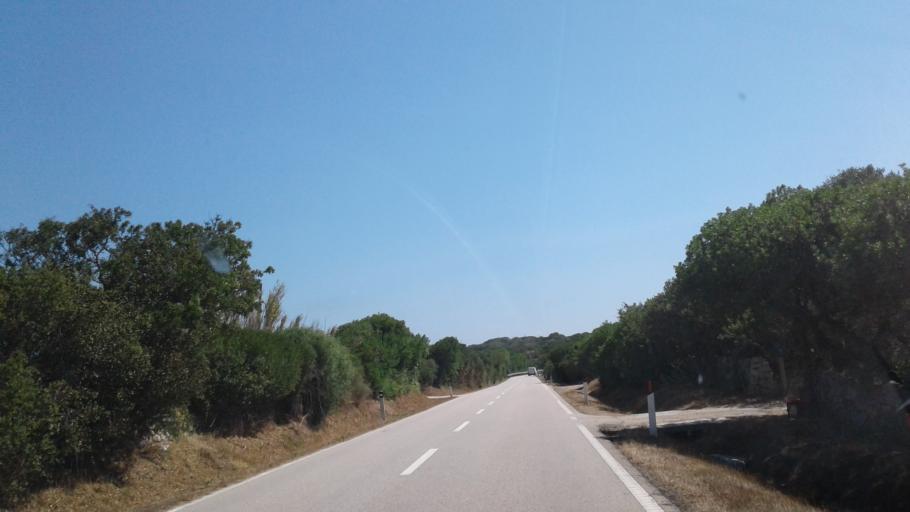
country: IT
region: Sardinia
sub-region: Provincia di Olbia-Tempio
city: Luogosanto
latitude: 41.1251
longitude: 9.2760
